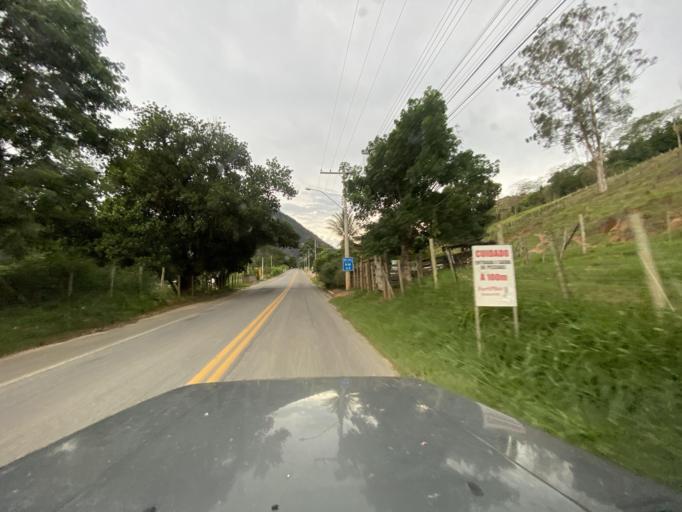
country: BR
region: Espirito Santo
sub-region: Jeronimo Monteiro
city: Jeronimo Monteiro
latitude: -20.7914
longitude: -41.3854
